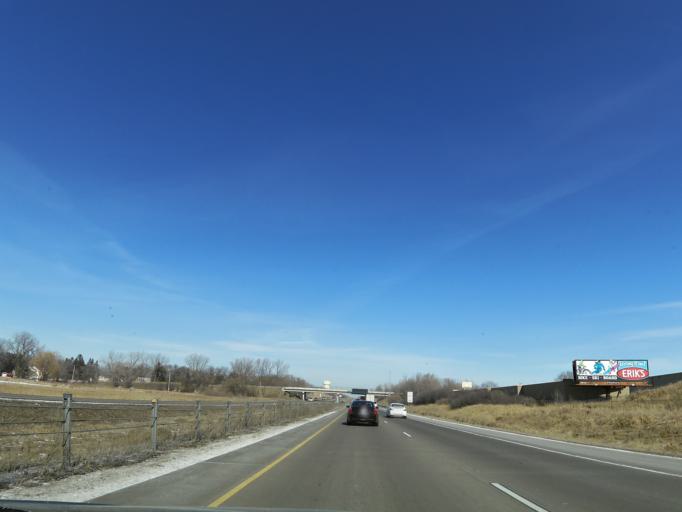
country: US
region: Minnesota
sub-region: Washington County
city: Oakdale
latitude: 44.9677
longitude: -92.9583
